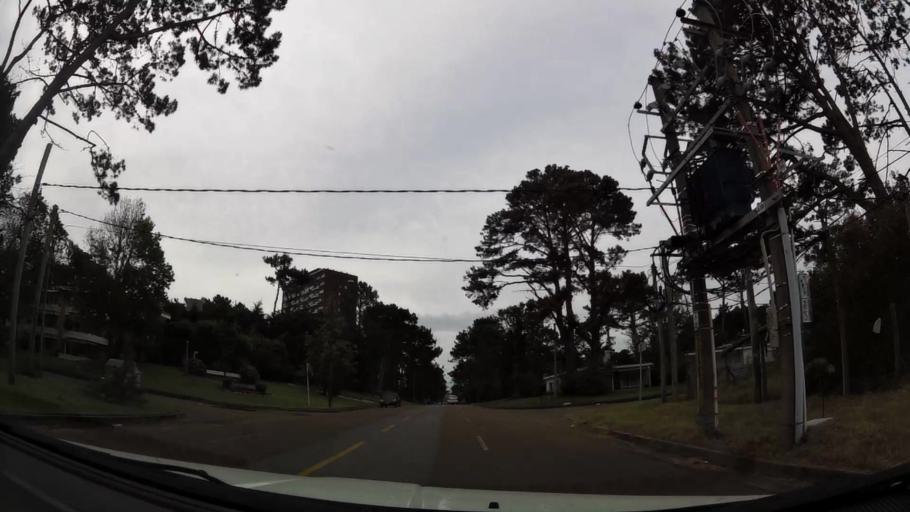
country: UY
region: Maldonado
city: Maldonado
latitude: -34.9280
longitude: -54.9532
